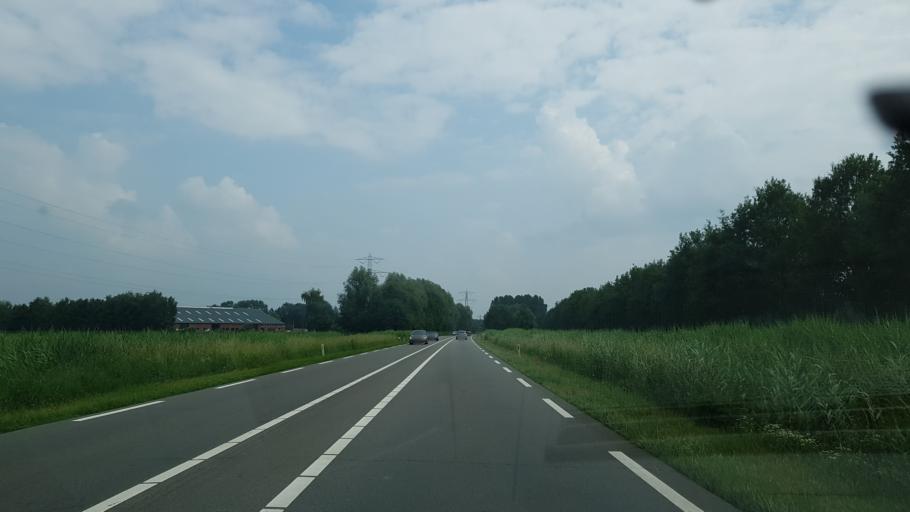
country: NL
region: North Brabant
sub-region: Gemeente Helmond
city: Helmond
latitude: 51.5025
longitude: 5.6738
